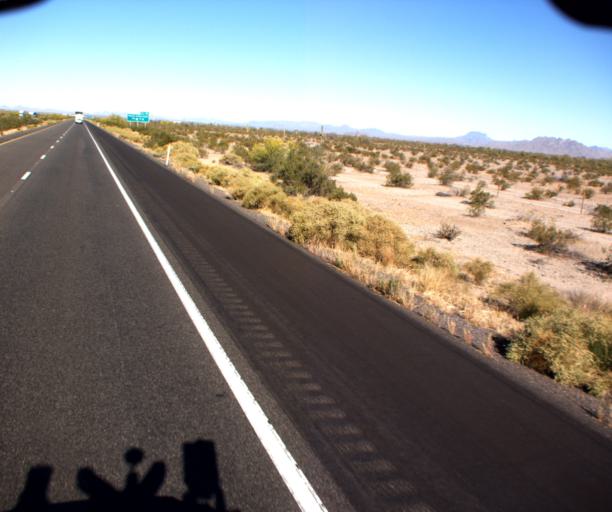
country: US
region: Arizona
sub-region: Maricopa County
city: Gila Bend
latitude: 32.9182
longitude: -112.6381
